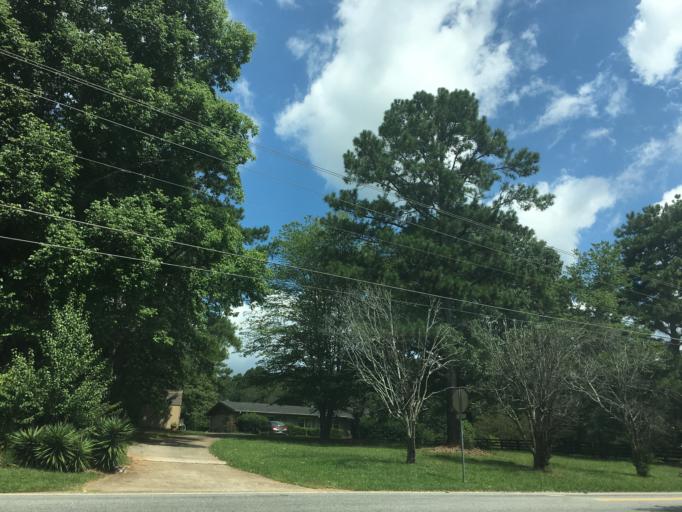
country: US
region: Georgia
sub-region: Fulton County
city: Roswell
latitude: 34.0901
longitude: -84.3772
